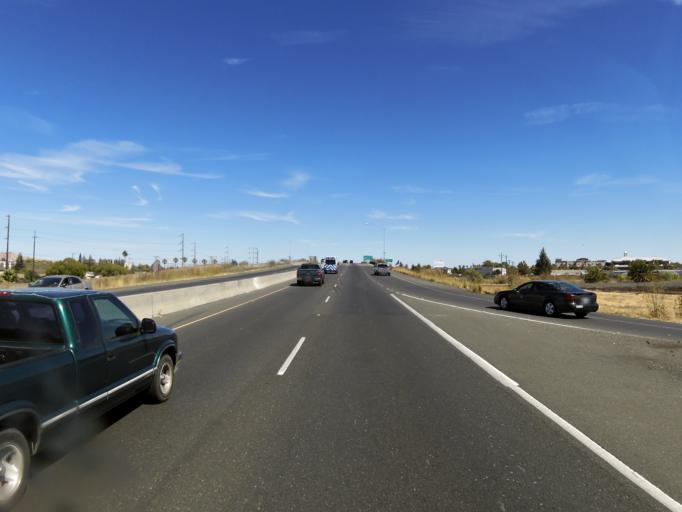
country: US
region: California
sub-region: Solano County
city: Suisun
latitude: 38.2425
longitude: -122.0452
